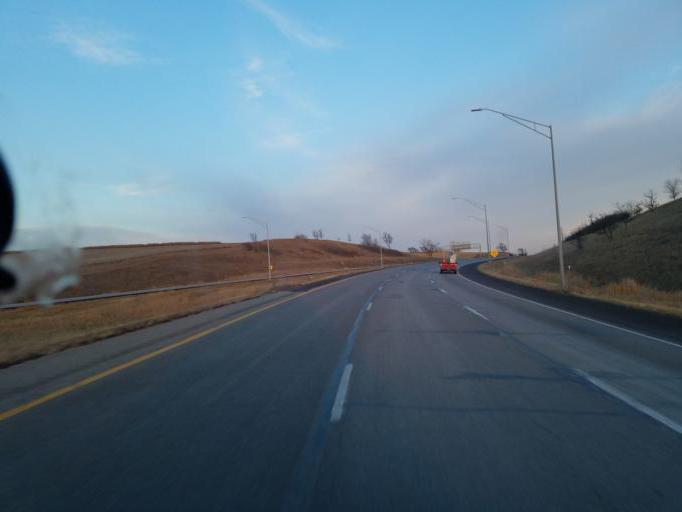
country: US
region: Iowa
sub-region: Pottawattamie County
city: Avoca
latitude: 41.4984
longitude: -95.5782
